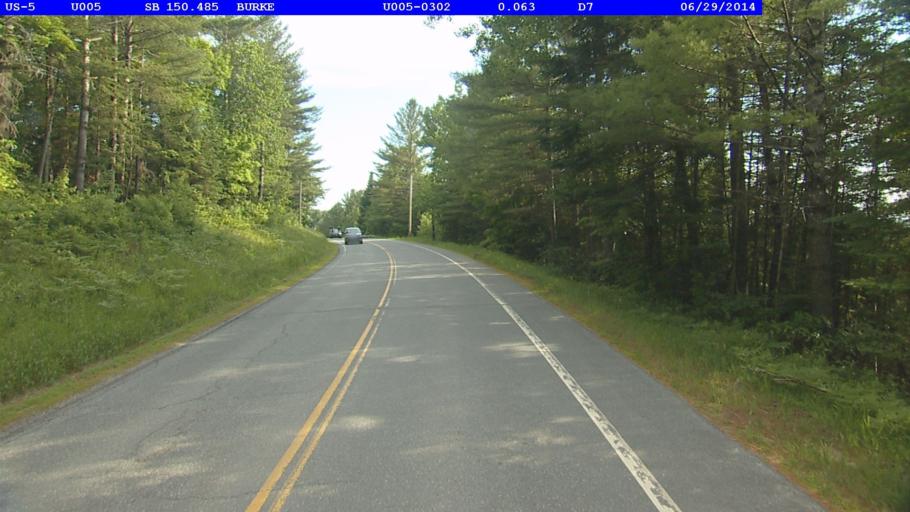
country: US
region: Vermont
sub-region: Caledonia County
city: Lyndonville
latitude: 44.5885
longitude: -71.9815
